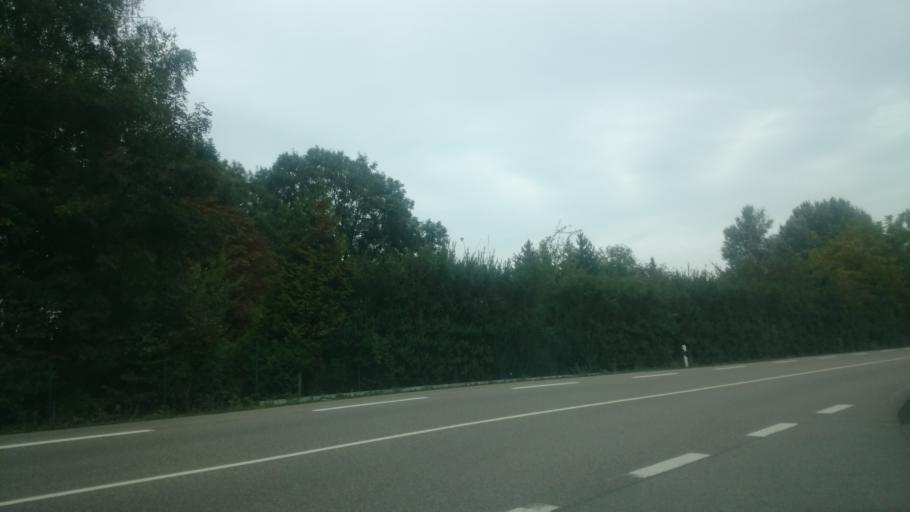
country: DE
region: Bavaria
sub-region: Swabia
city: Friedberg
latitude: 48.3965
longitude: 10.9486
